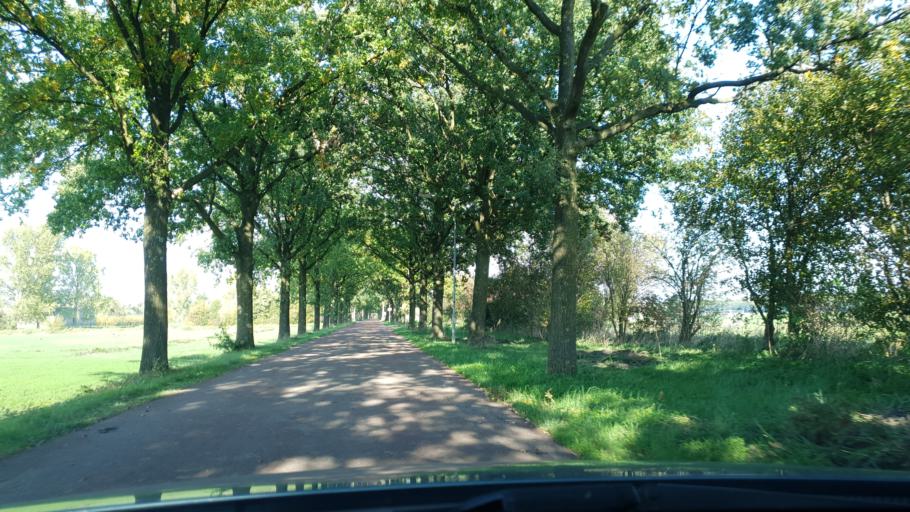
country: NL
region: Gelderland
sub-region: Gemeente Wijchen
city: Wijchen
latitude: 51.8338
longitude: 5.7458
